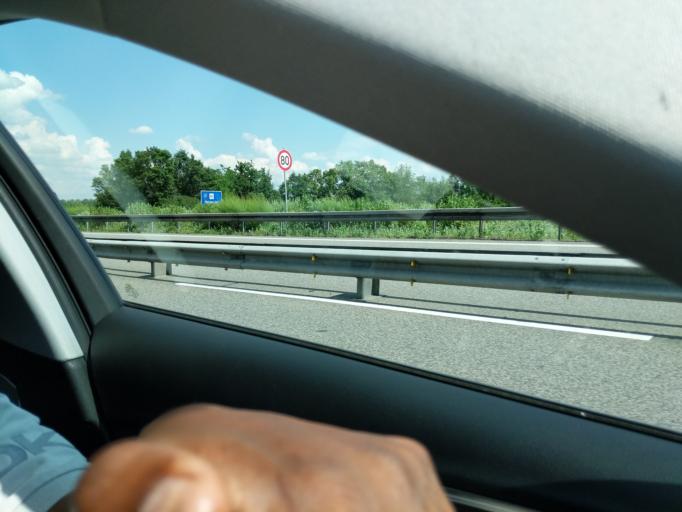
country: DE
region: Saxony-Anhalt
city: Vockerode
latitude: 51.8616
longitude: 12.3557
